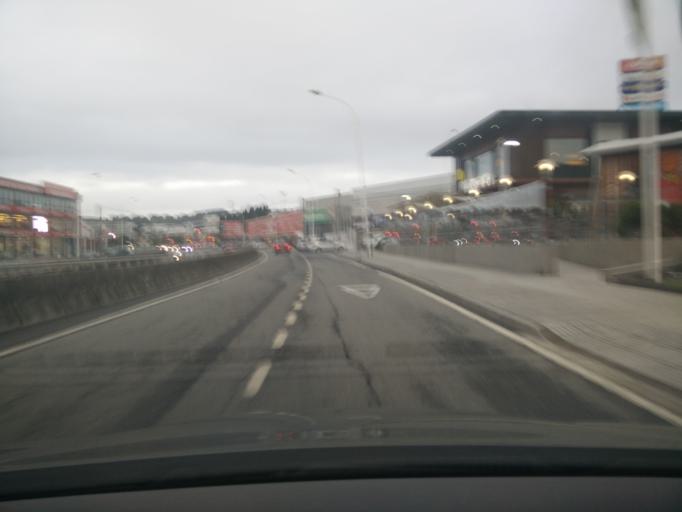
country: ES
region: Galicia
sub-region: Provincia da Coruna
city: A Coruna
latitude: 43.3494
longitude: -8.4207
